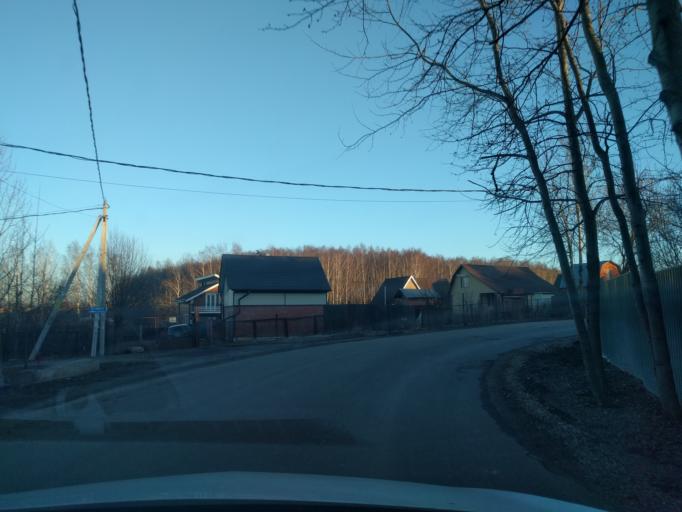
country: RU
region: Moskovskaya
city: Dubrovitsy
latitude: 55.4888
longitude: 37.4426
